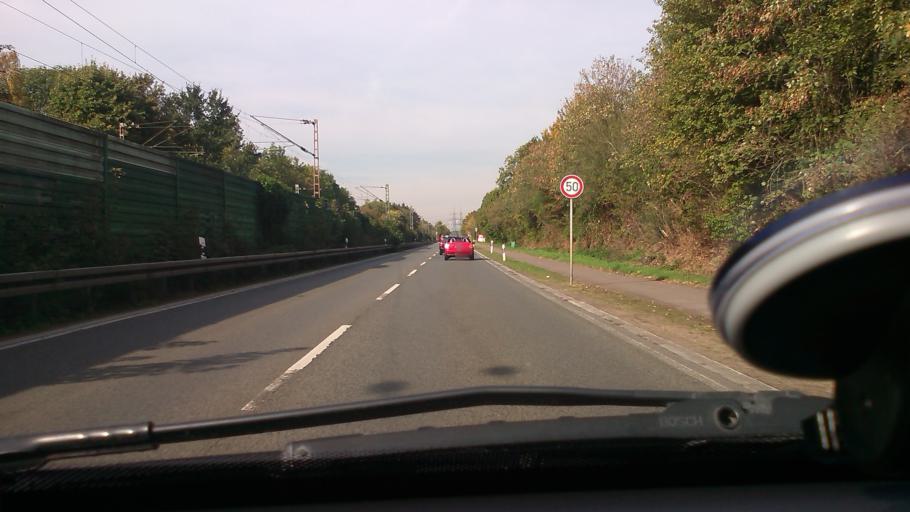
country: DE
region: North Rhine-Westphalia
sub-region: Regierungsbezirk Dusseldorf
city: Langenfeld
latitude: 51.1293
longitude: 6.9498
